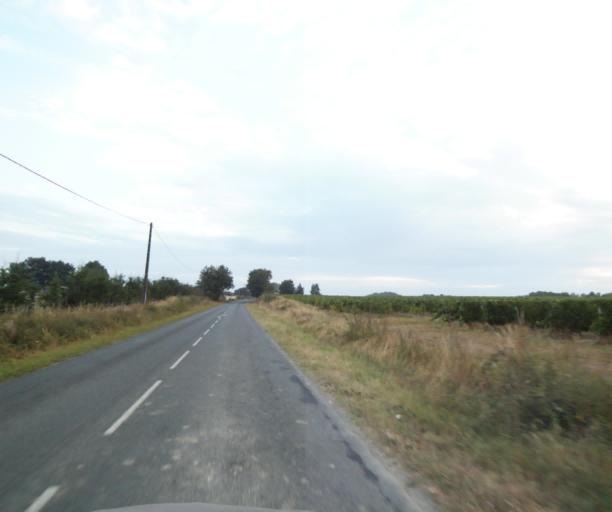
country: FR
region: Aquitaine
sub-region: Departement de la Gironde
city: La Sauve
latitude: 44.7534
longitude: -0.3309
